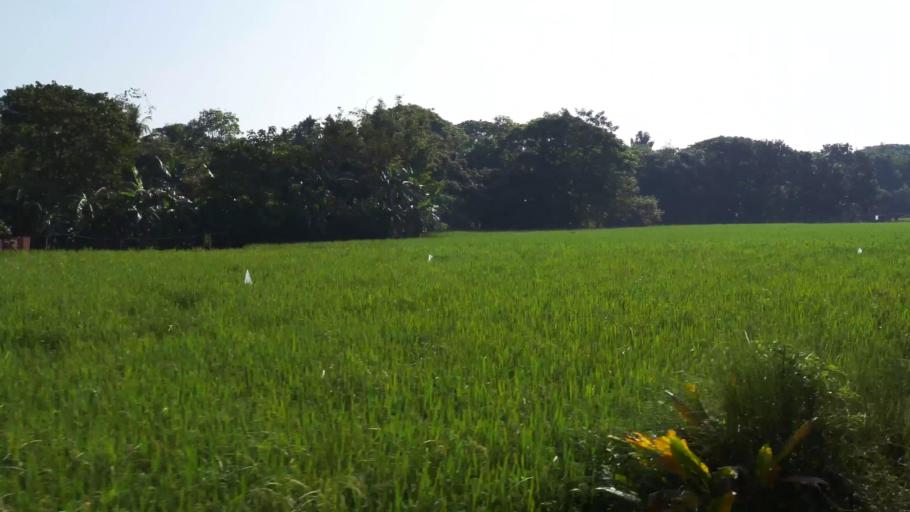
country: BD
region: Dhaka
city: Muktagacha
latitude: 24.8069
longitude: 90.3022
